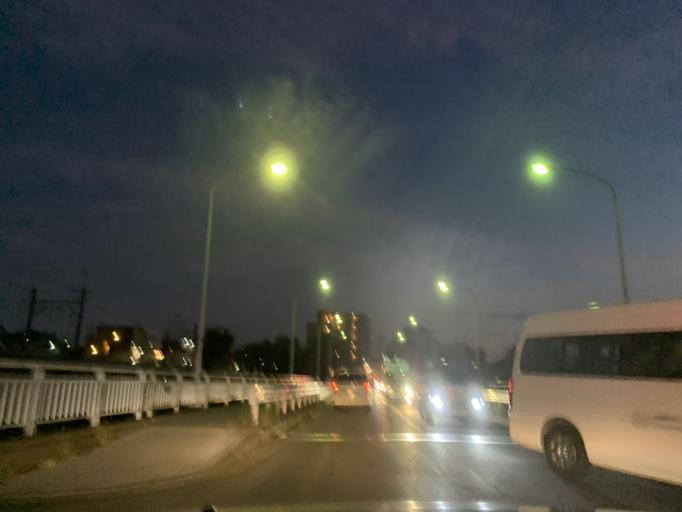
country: JP
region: Chiba
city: Noda
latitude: 35.9163
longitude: 139.9053
